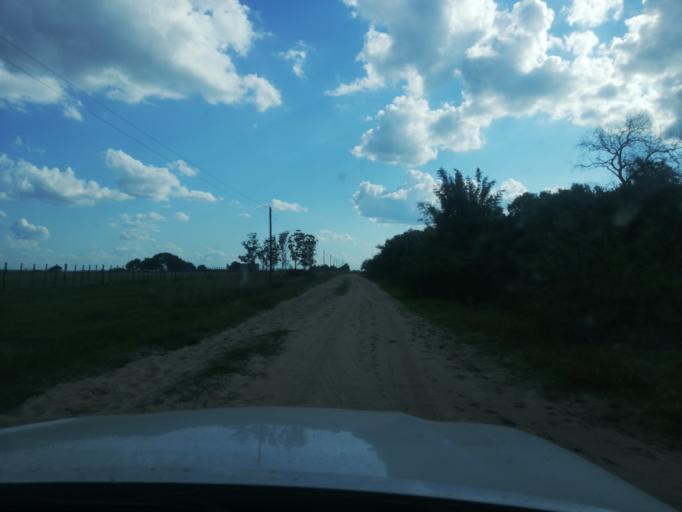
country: AR
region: Corrientes
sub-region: Departamento de San Miguel
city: San Miguel
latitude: -27.9952
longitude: -57.5782
